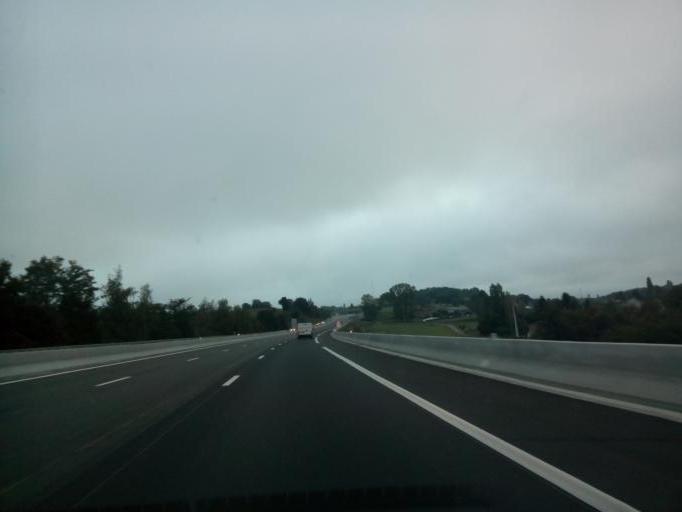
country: FR
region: Rhone-Alpes
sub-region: Departement de l'Isere
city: Saint-Didier-de-la-Tour
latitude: 45.5611
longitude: 5.4749
